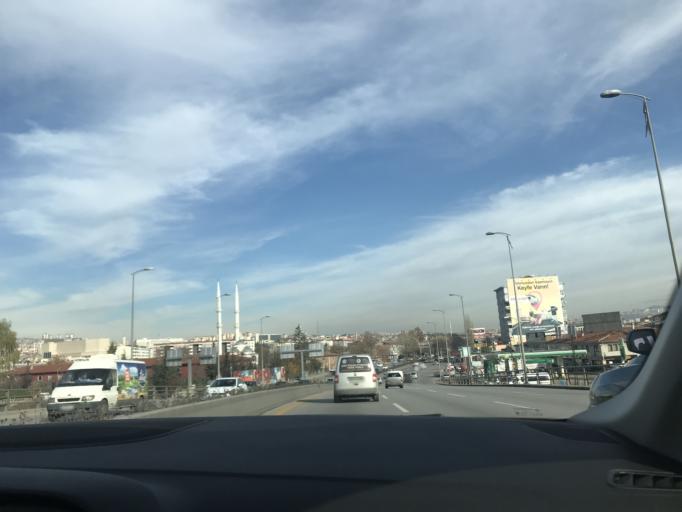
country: TR
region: Ankara
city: Ankara
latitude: 39.9517
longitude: 32.8360
